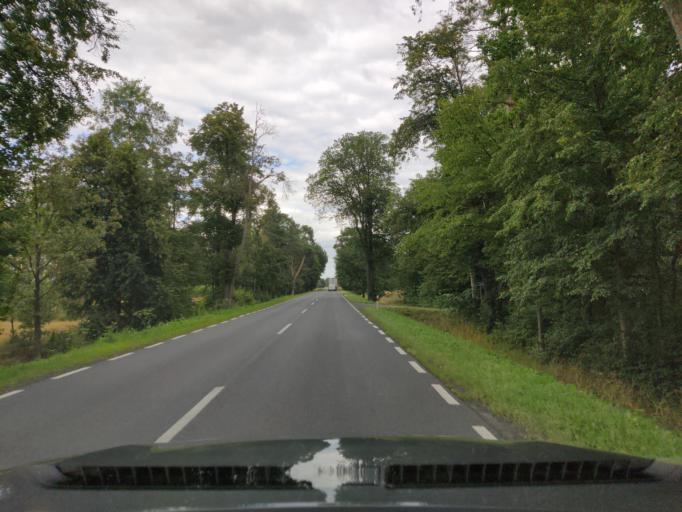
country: PL
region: Masovian Voivodeship
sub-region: Powiat sokolowski
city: Ceranow
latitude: 52.6548
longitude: 22.2708
